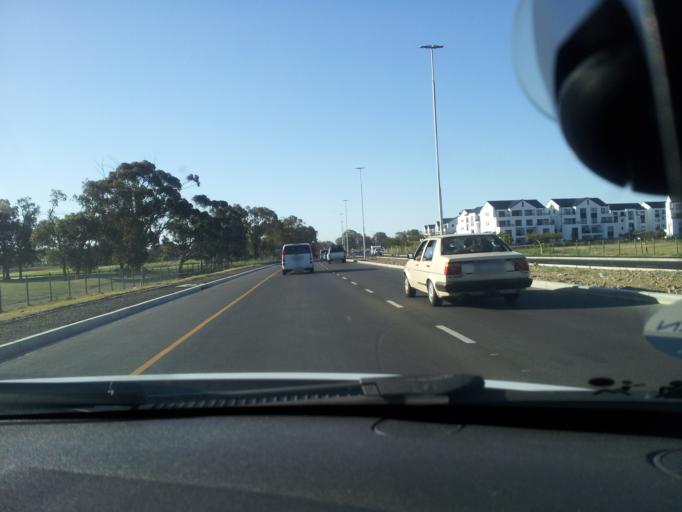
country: ZA
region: Western Cape
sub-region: Cape Winelands District Municipality
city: Stellenbosch
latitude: -34.0946
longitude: 18.8218
